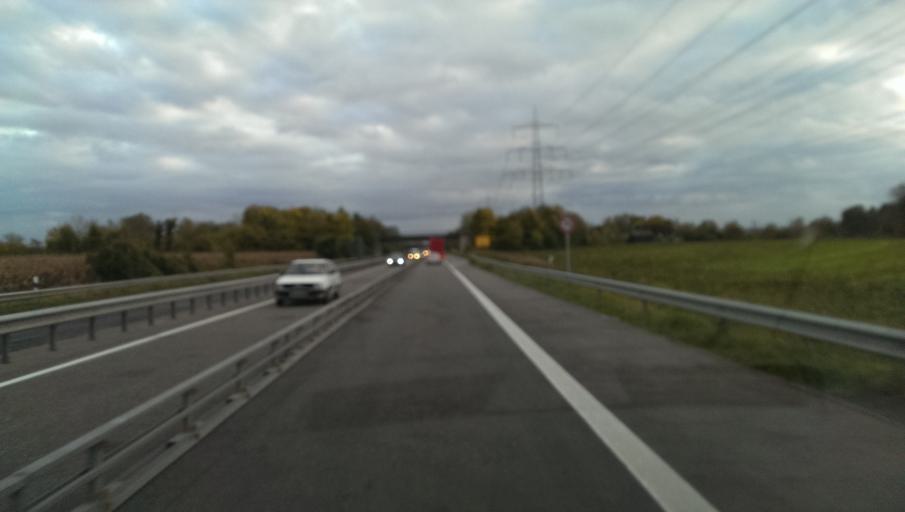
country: DE
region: Rheinland-Pfalz
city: Jockgrim
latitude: 49.0741
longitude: 8.2862
